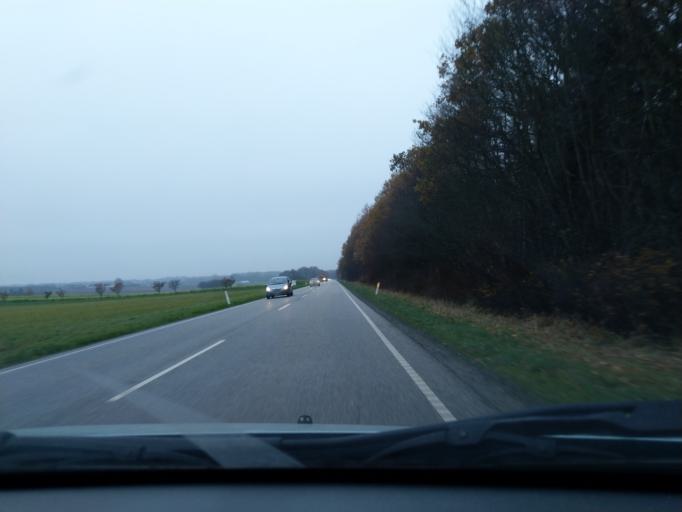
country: DK
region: Zealand
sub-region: Vordingborg Kommune
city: Praesto
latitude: 55.1126
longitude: 12.0544
